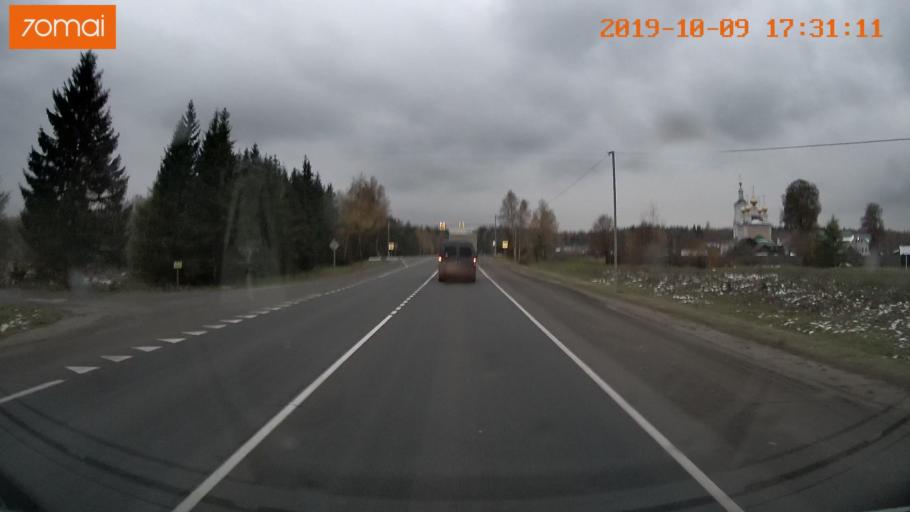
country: RU
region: Ivanovo
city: Bogorodskoye
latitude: 57.1373
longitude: 41.0418
